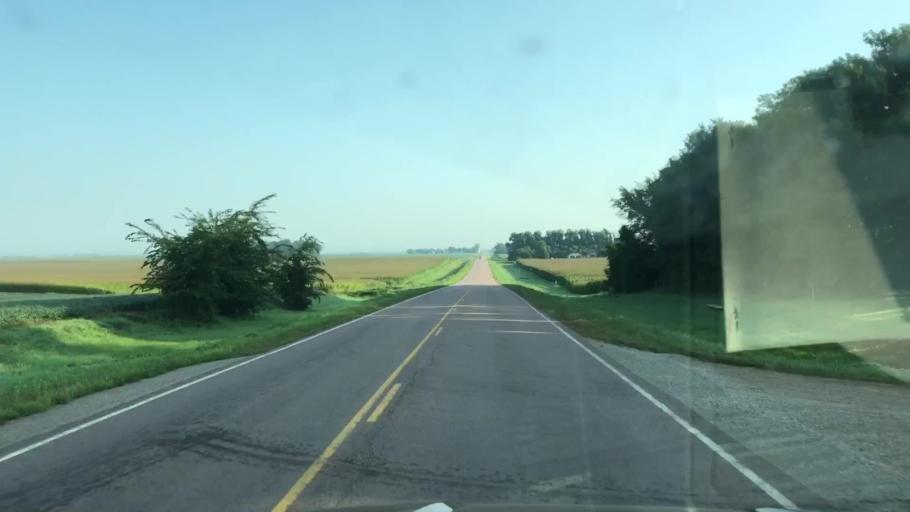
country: US
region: Iowa
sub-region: Lyon County
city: George
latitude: 43.2936
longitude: -95.9994
